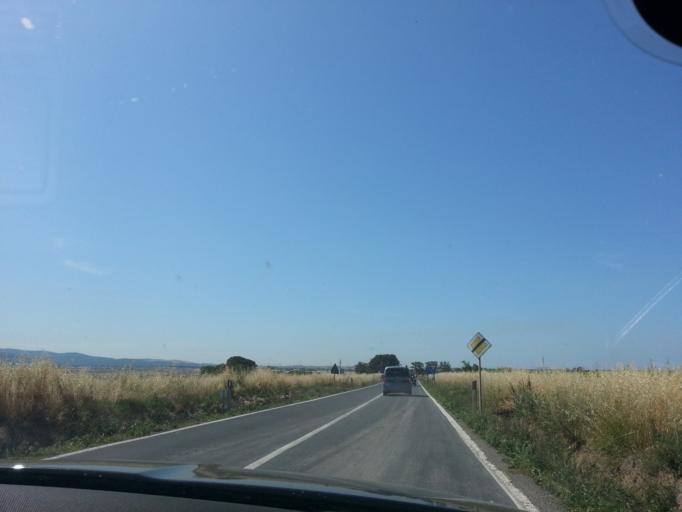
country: IT
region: Latium
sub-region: Provincia di Viterbo
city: Tarquinia
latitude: 42.2120
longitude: 11.7817
